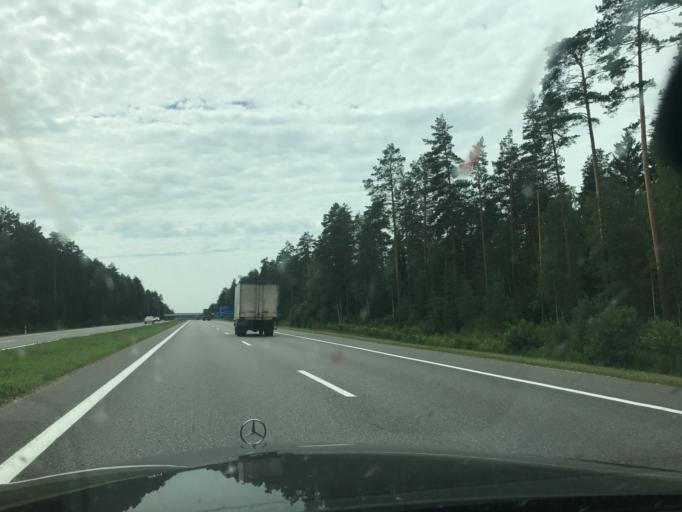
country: BY
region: Minsk
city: Zamostochcha
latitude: 53.8985
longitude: 27.9447
